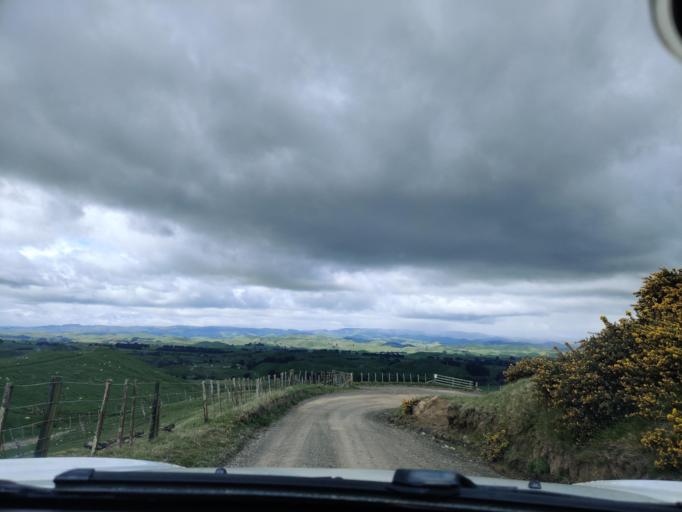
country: NZ
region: Manawatu-Wanganui
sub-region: Palmerston North City
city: Palmerston North
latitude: -40.2856
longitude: 175.8635
